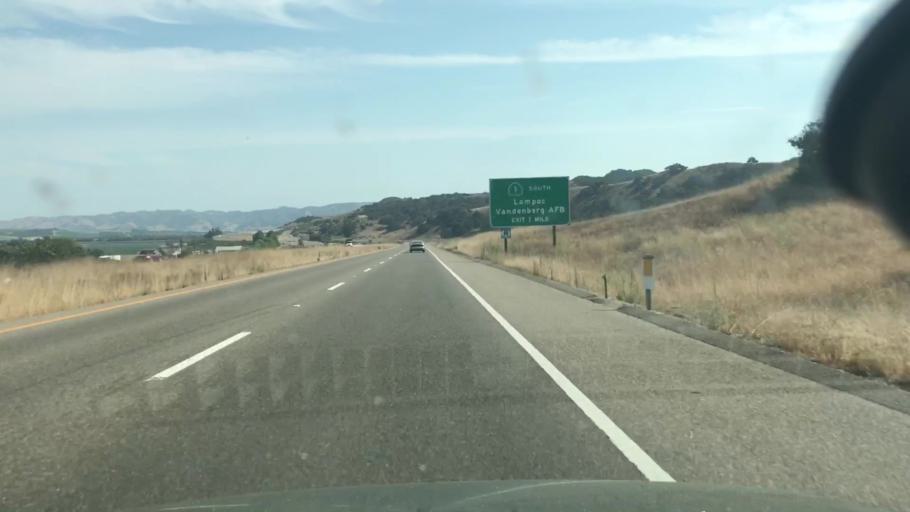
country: US
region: California
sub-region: Santa Barbara County
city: Orcutt
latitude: 34.8156
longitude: -120.4494
